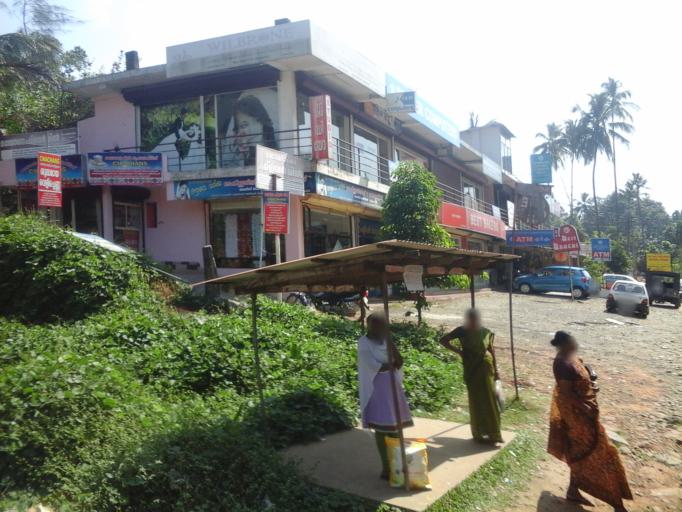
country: IN
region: Kerala
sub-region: Kottayam
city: Erattupetta
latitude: 9.7000
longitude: 76.7587
